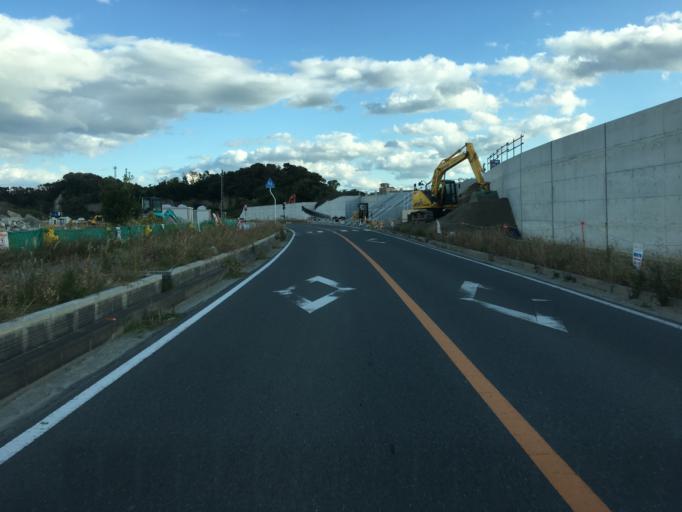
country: JP
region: Miyagi
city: Marumori
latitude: 37.8284
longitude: 140.9656
